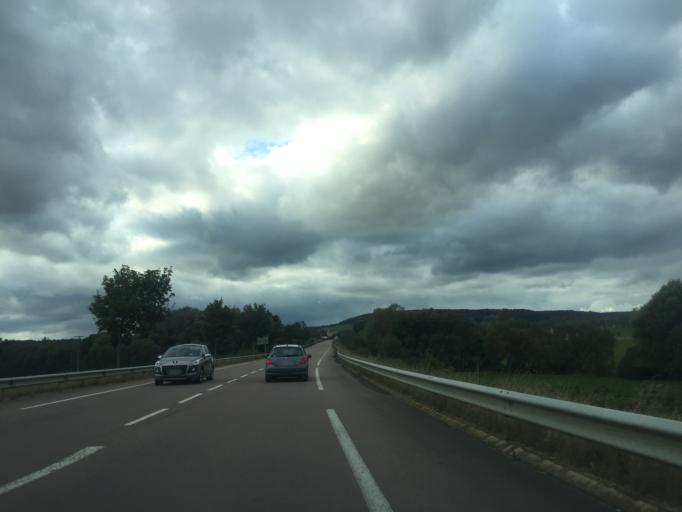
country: FR
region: Lorraine
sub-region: Departement des Vosges
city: Chatenois
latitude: 48.2956
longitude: 5.8620
